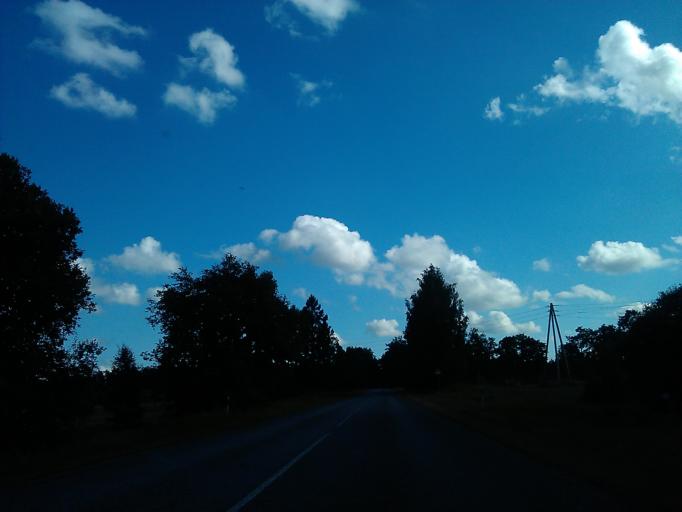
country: LV
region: Valmieras Rajons
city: Valmiera
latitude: 57.6859
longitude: 25.4300
